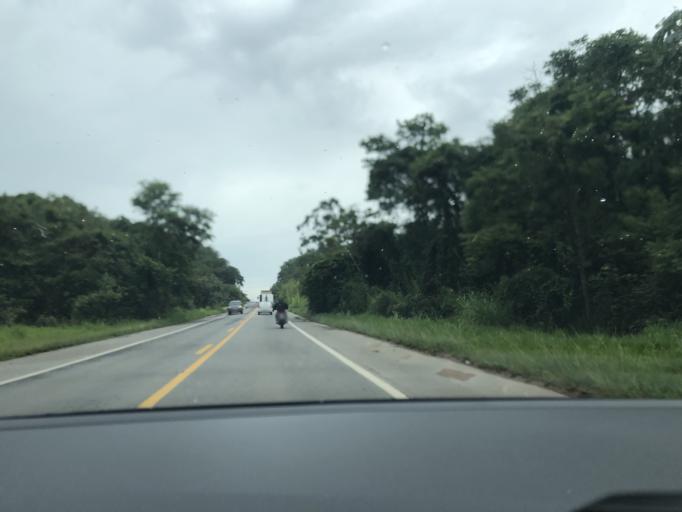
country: BR
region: Sao Paulo
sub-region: Jarinu
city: Jarinu
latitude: -23.1497
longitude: -46.7450
